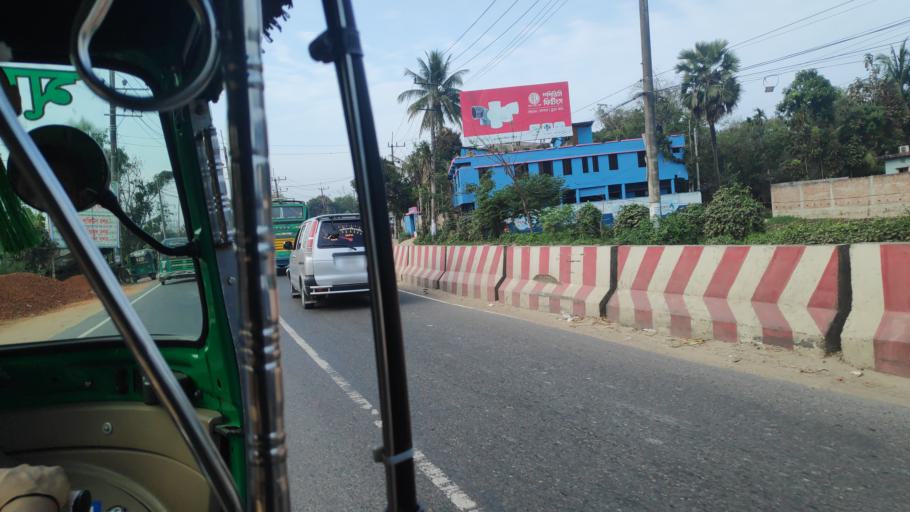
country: BD
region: Chittagong
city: Raojan
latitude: 22.4878
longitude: 91.8081
